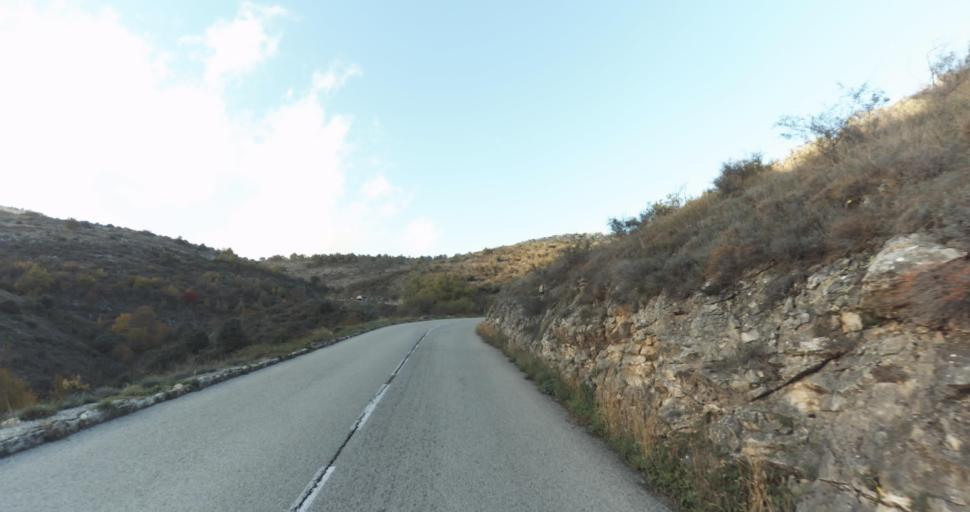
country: FR
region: Provence-Alpes-Cote d'Azur
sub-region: Departement des Alpes-Maritimes
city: Vence
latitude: 43.7509
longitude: 7.0959
